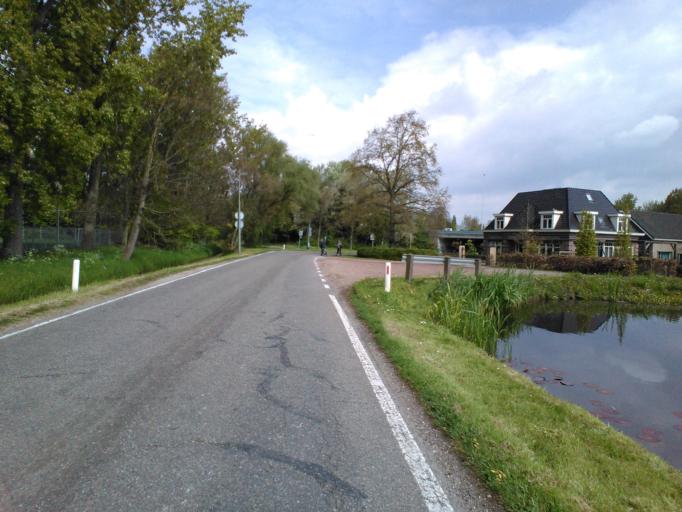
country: NL
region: South Holland
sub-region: Gemeente Maassluis
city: Maassluis
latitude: 51.9226
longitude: 4.2734
